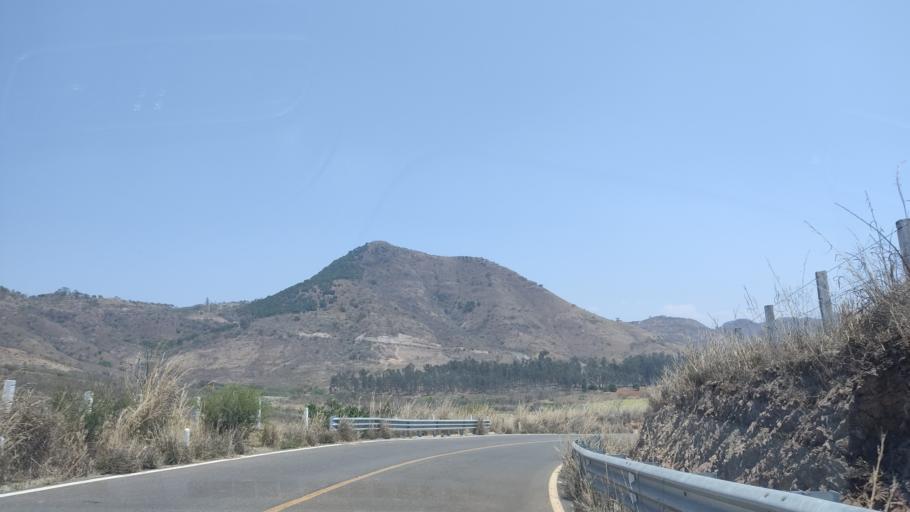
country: MX
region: Nayarit
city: Puga
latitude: 21.6104
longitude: -104.7266
